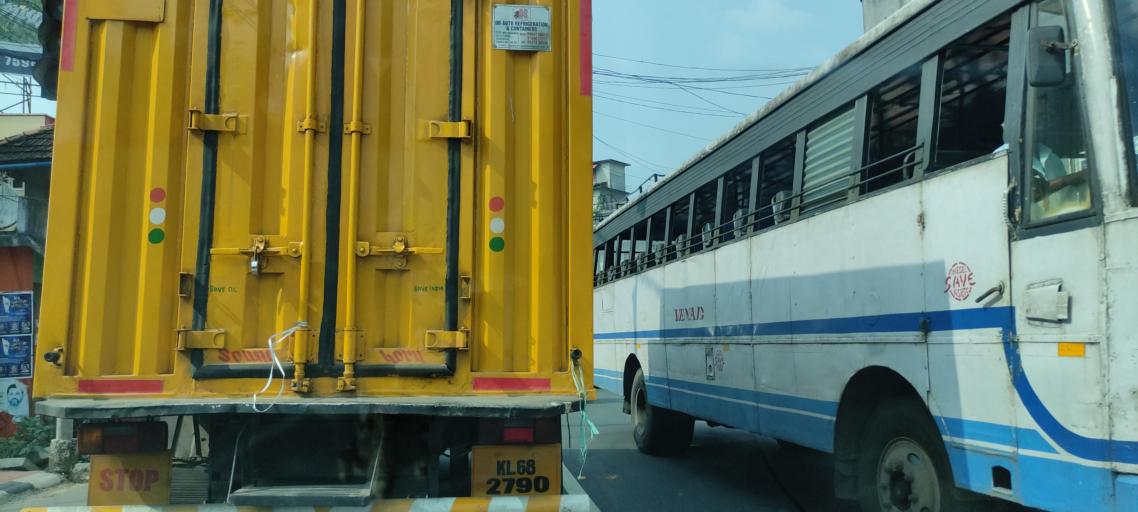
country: IN
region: Kerala
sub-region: Alappuzha
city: Chengannur
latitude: 9.3146
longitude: 76.6176
